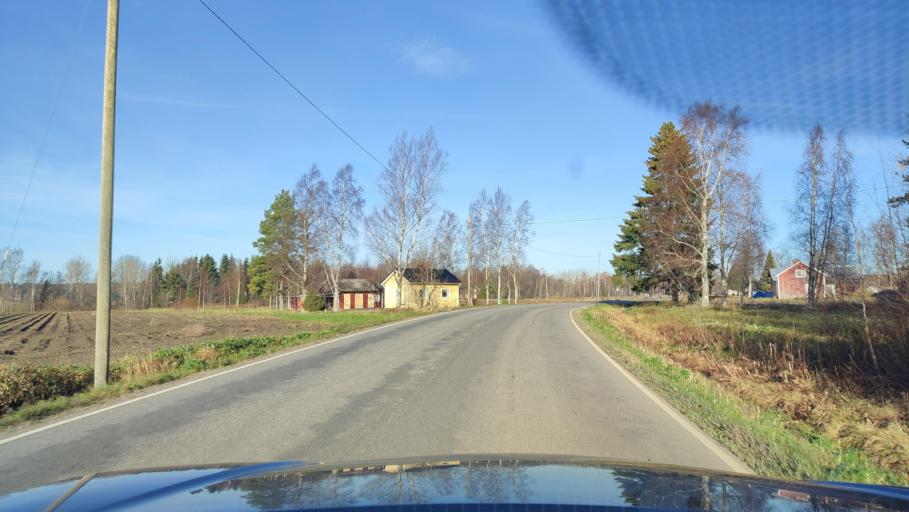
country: FI
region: Southern Ostrobothnia
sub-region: Suupohja
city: Karijoki
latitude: 62.2719
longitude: 21.7085
